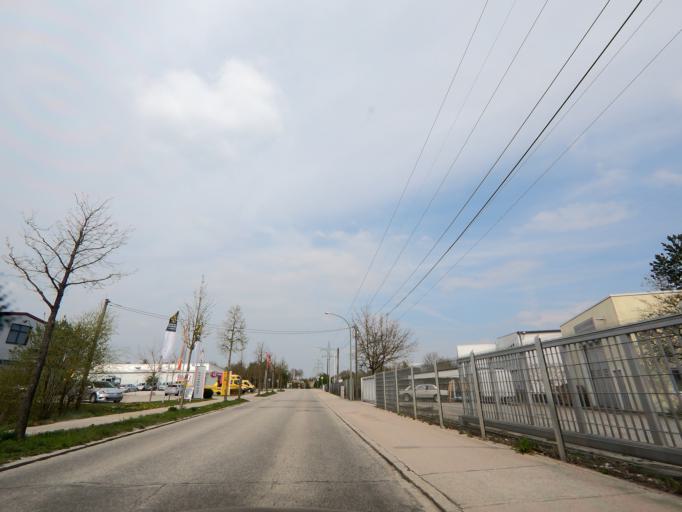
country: DE
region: Bavaria
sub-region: Lower Bavaria
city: Ergolding
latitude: 48.5630
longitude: 12.1394
